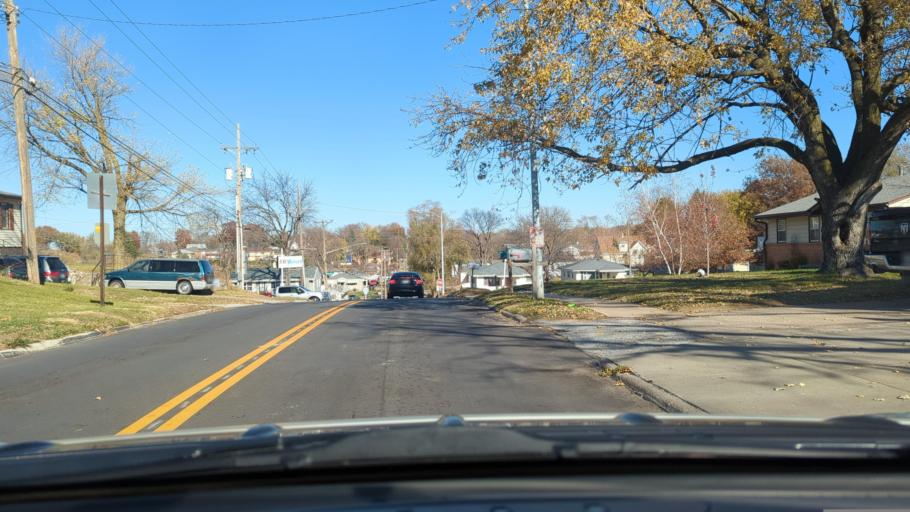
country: US
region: Nebraska
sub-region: Sarpy County
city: La Vista
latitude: 41.1900
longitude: -95.9770
